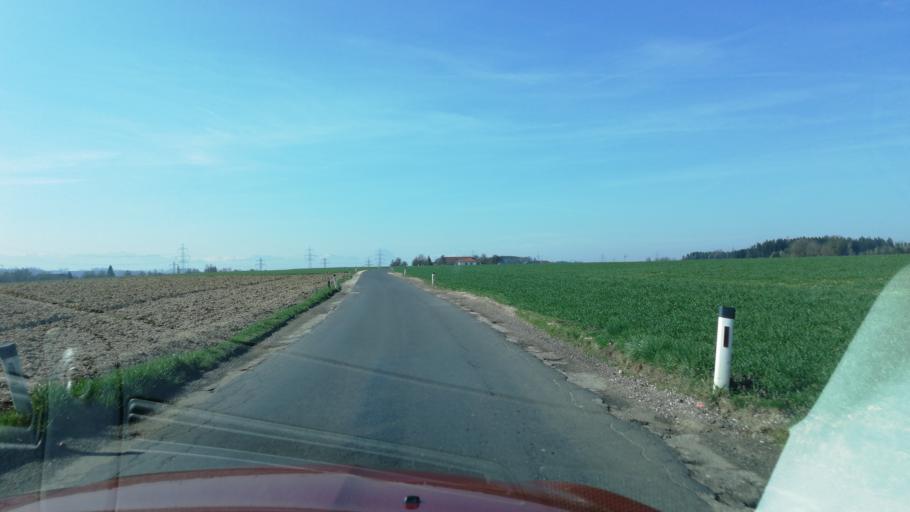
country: AT
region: Upper Austria
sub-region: Politischer Bezirk Kirchdorf an der Krems
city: Kremsmunster
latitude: 48.0965
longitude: 14.1051
